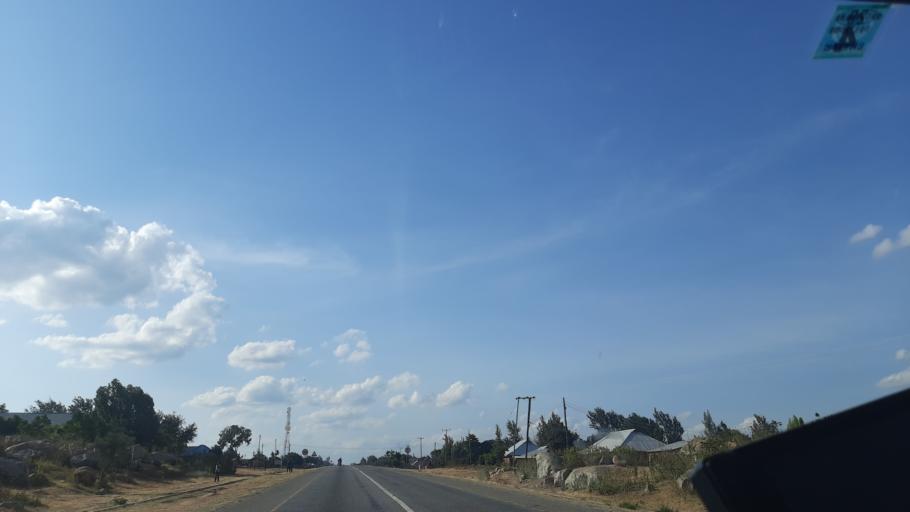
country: TZ
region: Singida
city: Puma
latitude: -5.0084
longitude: 34.7574
